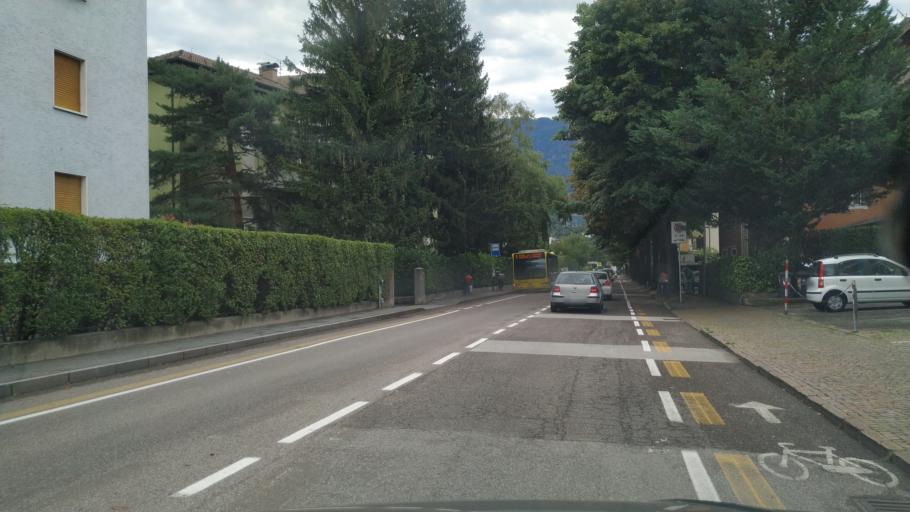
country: IT
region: Trentino-Alto Adige
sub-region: Bolzano
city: Tirolo
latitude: 46.6779
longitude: 11.1447
